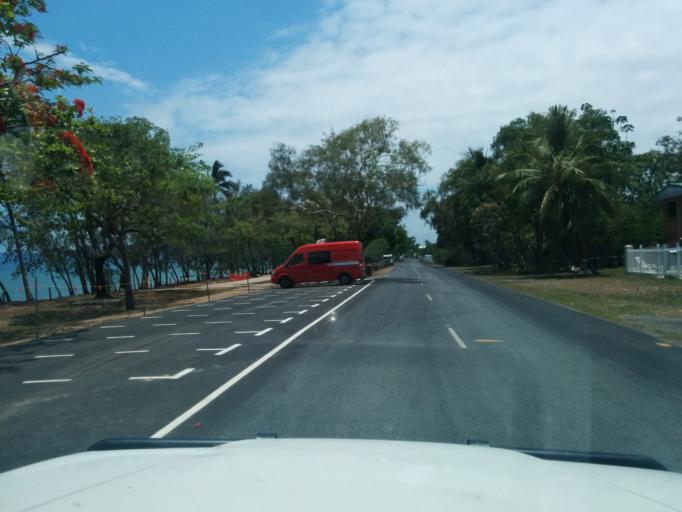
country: AU
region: Queensland
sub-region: Cairns
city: Yorkeys Knob
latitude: -16.8328
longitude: 145.7368
